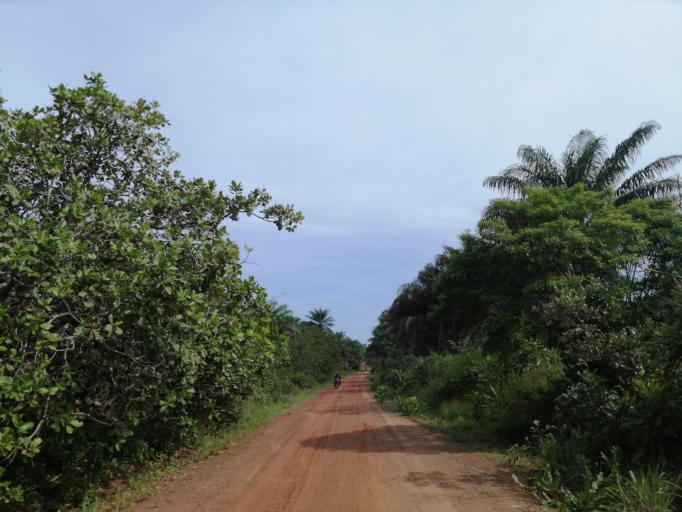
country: SL
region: Northern Province
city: Port Loko
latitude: 8.7751
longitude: -12.9171
